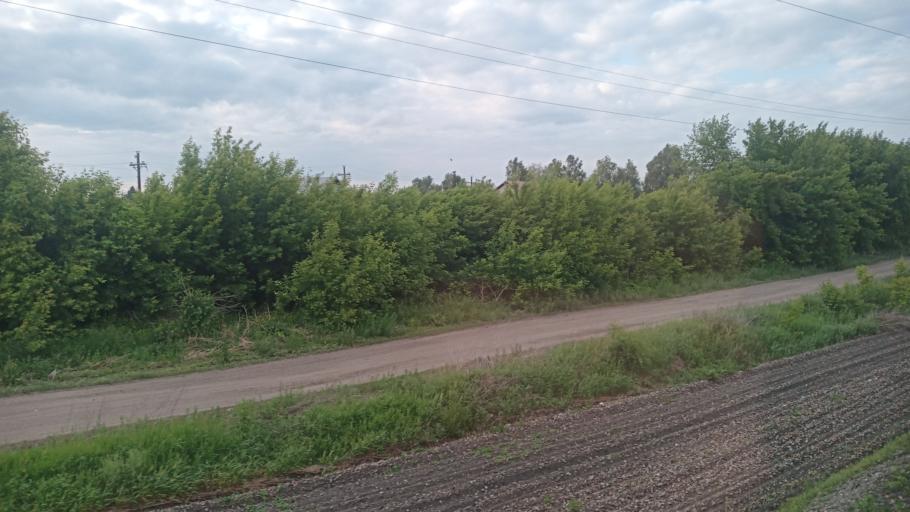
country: RU
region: Altai Krai
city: Novoaltaysk
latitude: 53.3792
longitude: 83.9313
